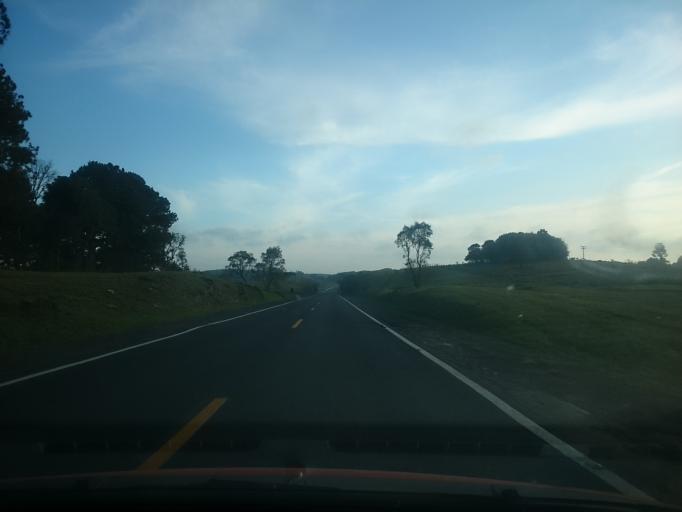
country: BR
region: Rio Grande do Sul
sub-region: Vacaria
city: Estrela
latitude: -28.1584
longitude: -50.6658
